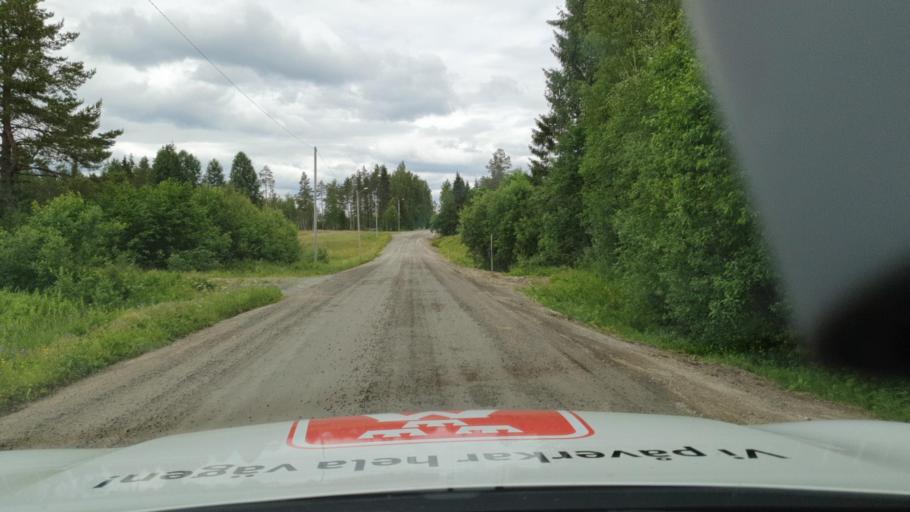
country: SE
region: Vaesterbotten
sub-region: Nordmalings Kommun
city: Nordmaling
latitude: 63.7167
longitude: 19.4281
